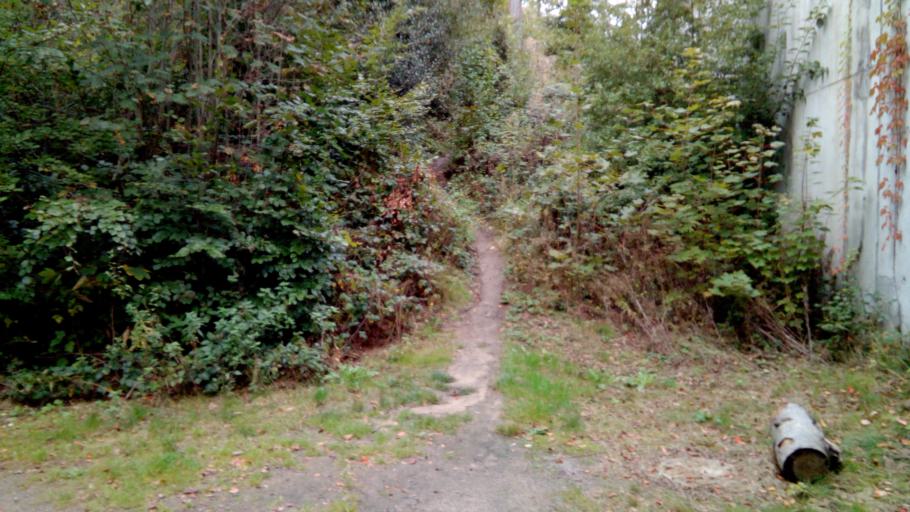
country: DE
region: North Rhine-Westphalia
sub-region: Regierungsbezirk Arnsberg
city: Bochum
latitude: 51.4415
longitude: 7.2562
